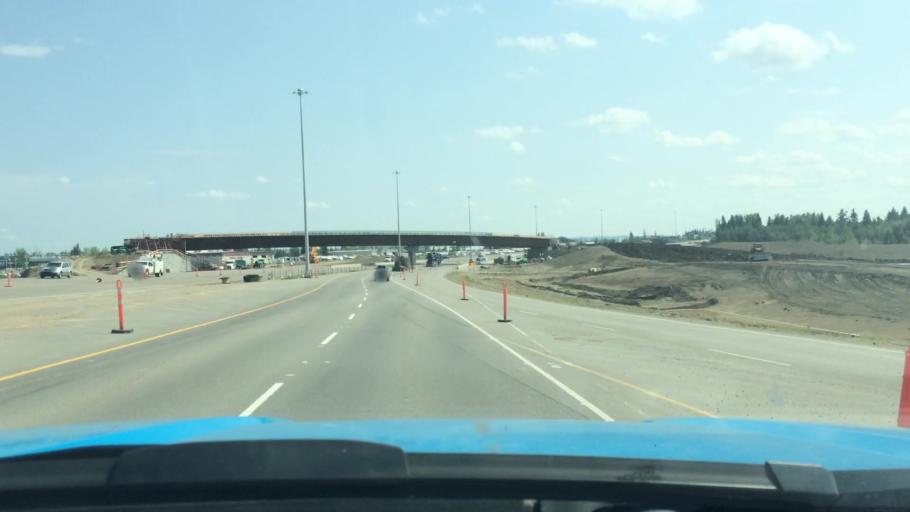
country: CA
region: Alberta
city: Red Deer
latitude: 52.2297
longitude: -113.8186
